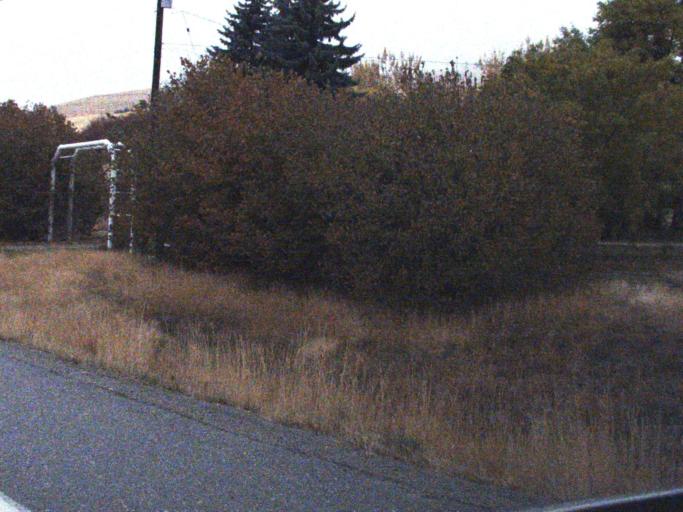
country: US
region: Washington
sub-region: Stevens County
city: Kettle Falls
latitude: 48.5966
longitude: -118.0048
